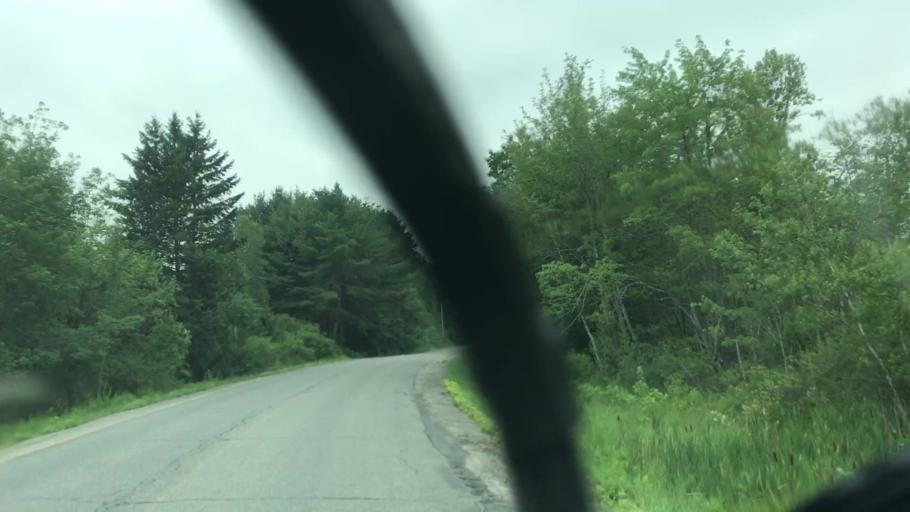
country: US
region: Maine
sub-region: Penobscot County
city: Veazie
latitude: 44.8670
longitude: -68.7168
